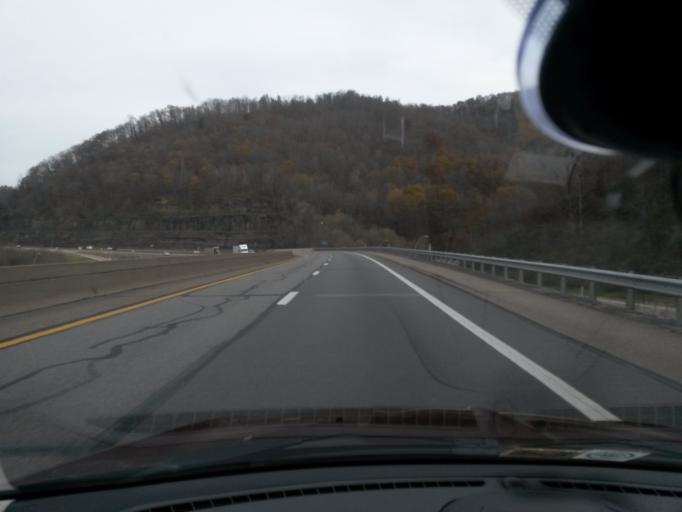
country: US
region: West Virginia
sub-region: Kanawha County
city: Chesapeake
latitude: 38.1565
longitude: -81.4461
